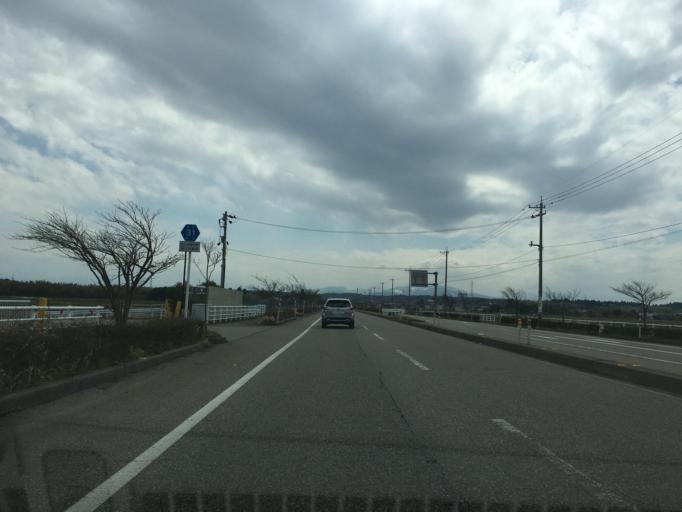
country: JP
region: Toyama
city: Kuragaki-kosugi
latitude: 36.7109
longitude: 137.1169
